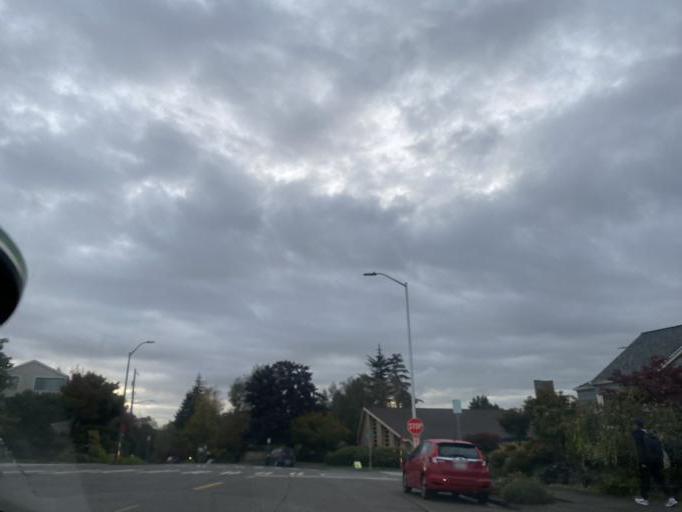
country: US
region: Washington
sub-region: King County
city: Seattle
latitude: 47.6353
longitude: -122.3936
